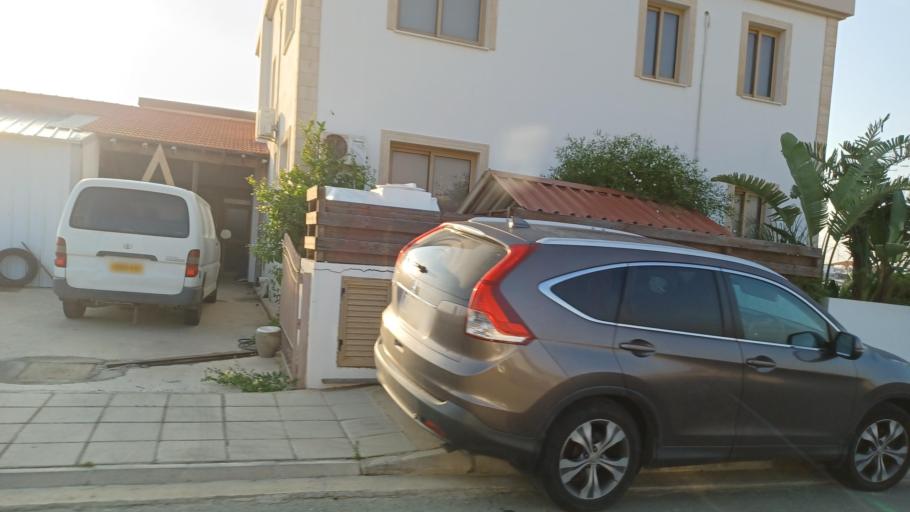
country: CY
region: Larnaka
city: Pyla
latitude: 35.0057
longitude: 33.6832
